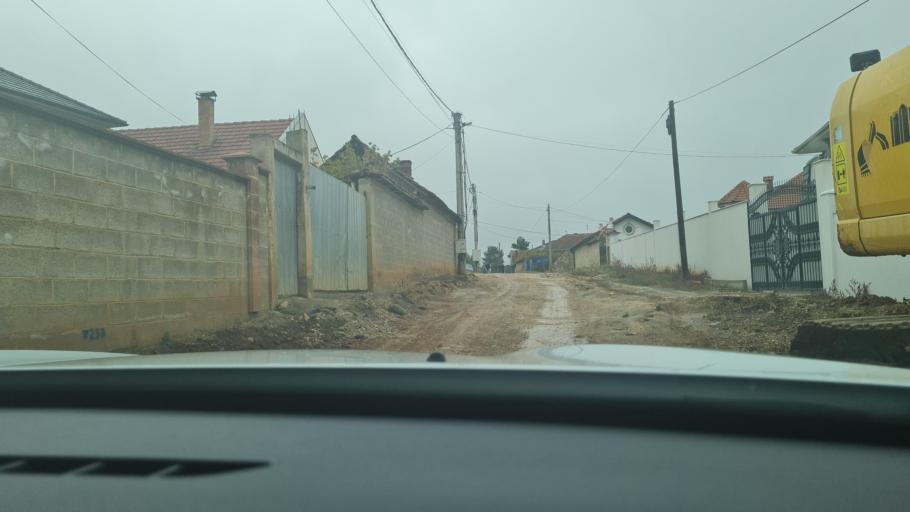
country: MK
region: Opstina Lipkovo
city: Matejche
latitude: 42.1214
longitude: 21.6019
